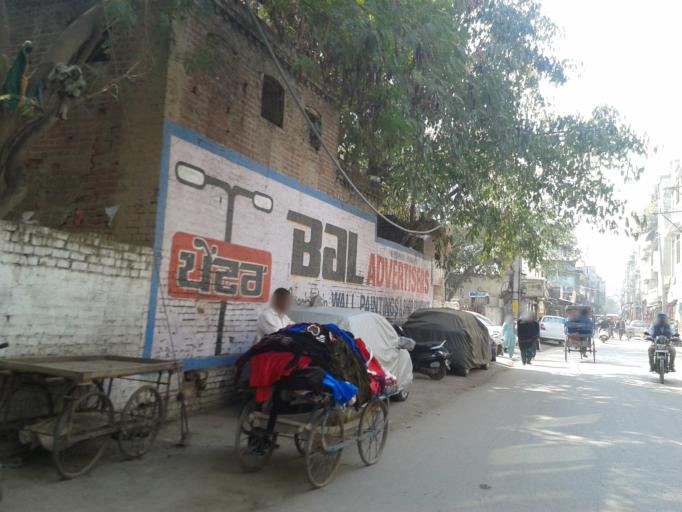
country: IN
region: Punjab
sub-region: Amritsar
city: Amritsar
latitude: 31.6267
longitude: 74.8819
